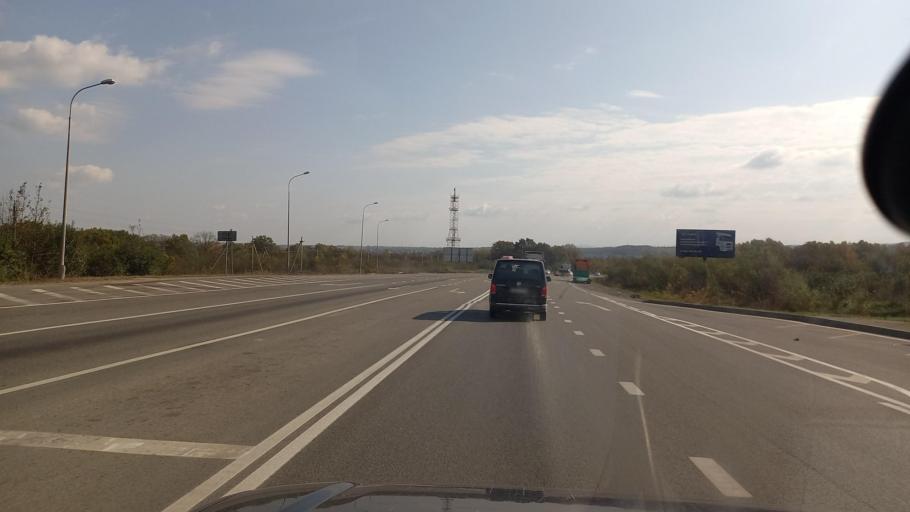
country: RU
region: Krasnodarskiy
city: Abinsk
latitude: 44.8484
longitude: 38.1428
